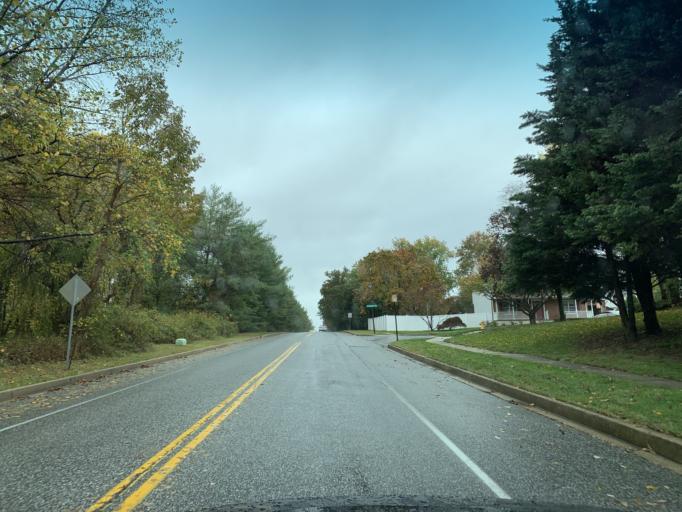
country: US
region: Maryland
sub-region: Harford County
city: South Bel Air
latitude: 39.5368
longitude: -76.3237
